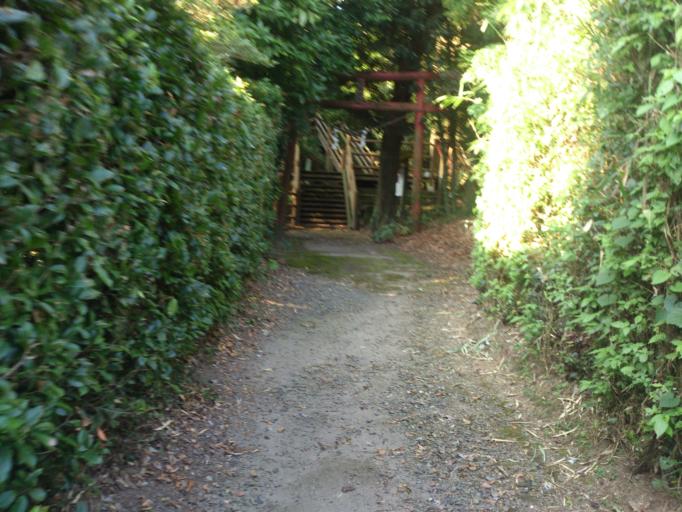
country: JP
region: Kagoshima
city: Kanoya
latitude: 31.3388
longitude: 130.9712
